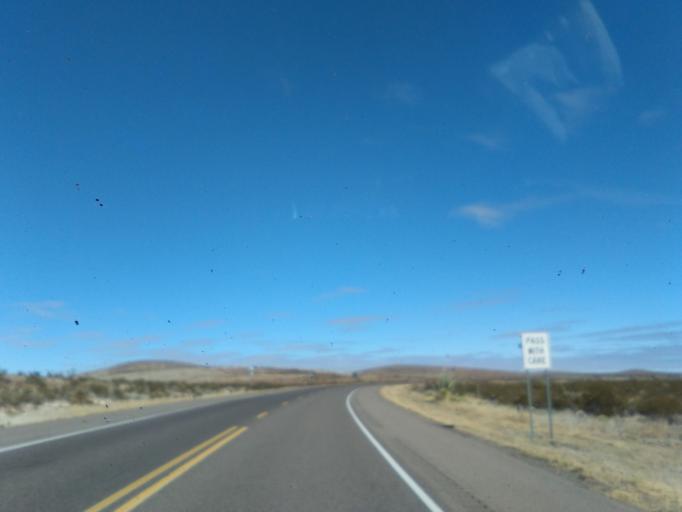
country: US
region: New Mexico
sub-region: Dona Ana County
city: Hatch
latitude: 32.5764
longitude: -107.4500
